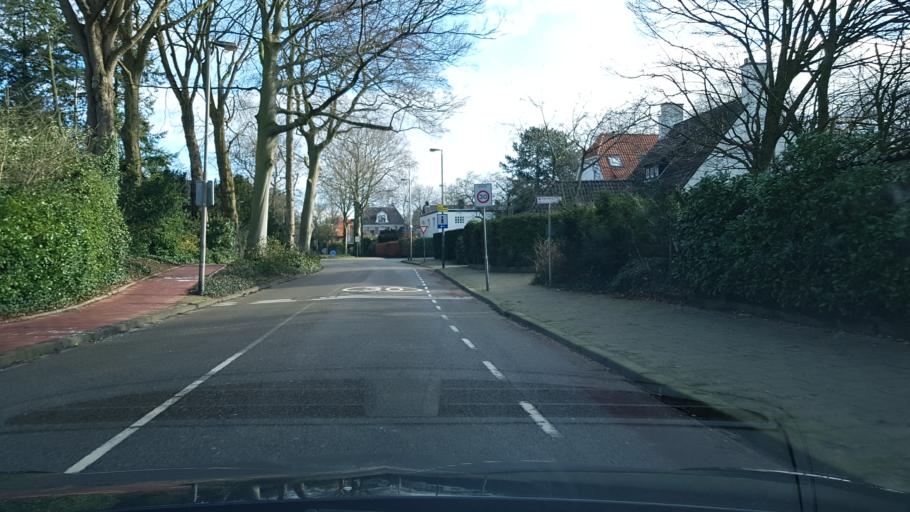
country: NL
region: North Holland
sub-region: Gemeente Bussum
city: Bussum
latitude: 52.2728
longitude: 5.1441
